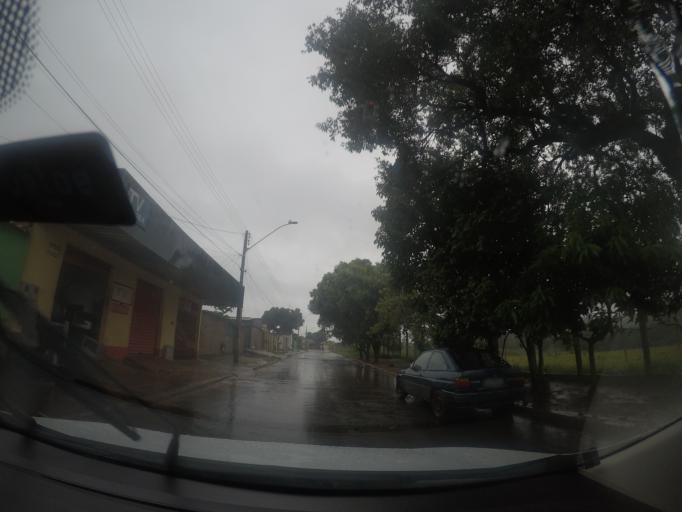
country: BR
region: Goias
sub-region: Goiania
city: Goiania
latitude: -16.6025
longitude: -49.3497
